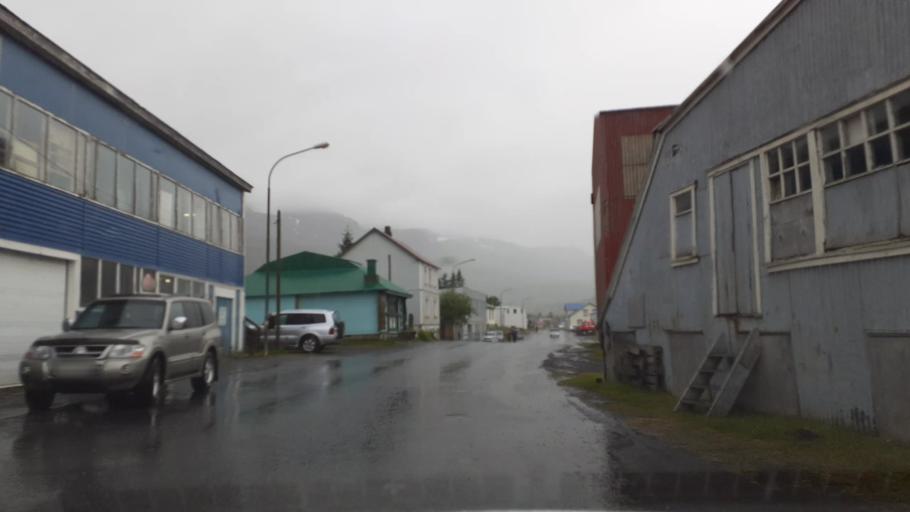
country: IS
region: East
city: Eskifjoerdur
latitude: 65.2653
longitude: -13.9921
